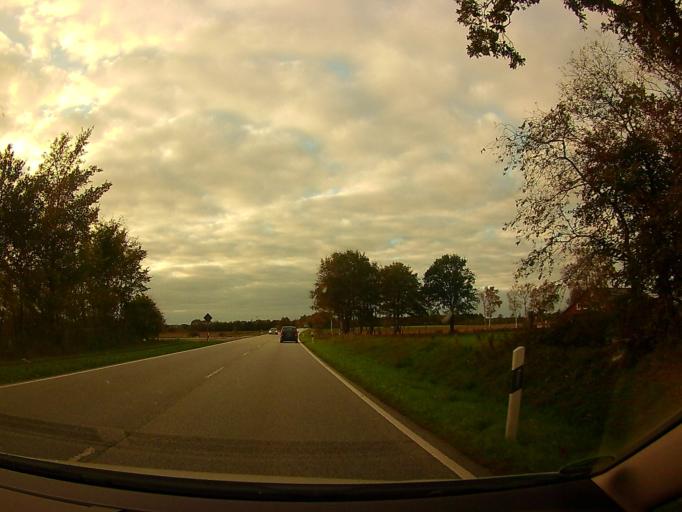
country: DE
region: Schleswig-Holstein
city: Silberstedt
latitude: 54.5163
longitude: 9.4071
